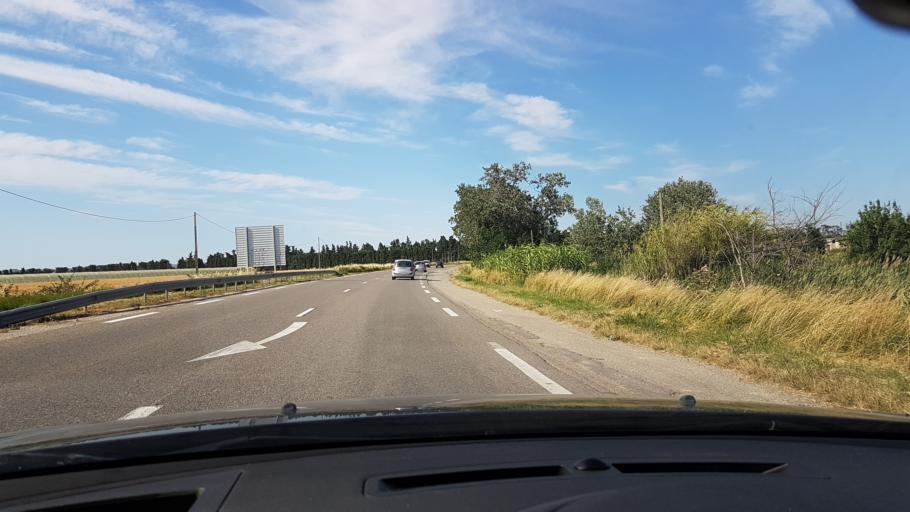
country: FR
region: Provence-Alpes-Cote d'Azur
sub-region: Departement des Bouches-du-Rhone
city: Saint-Etienne-du-Gres
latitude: 43.7702
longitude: 4.6918
